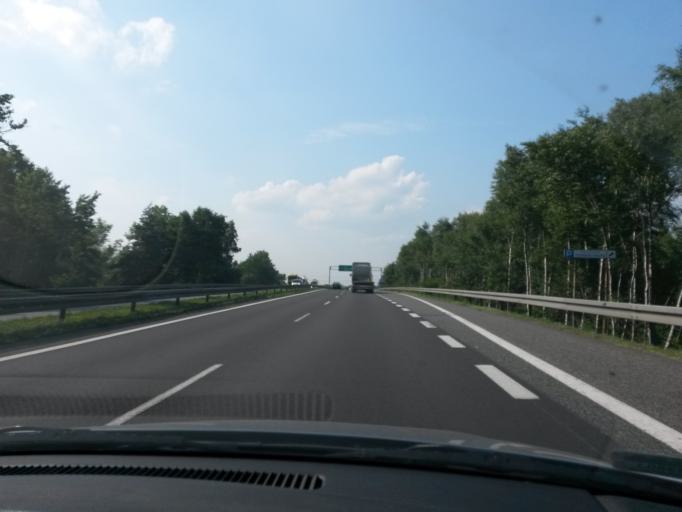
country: PL
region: Silesian Voivodeship
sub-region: Myslowice
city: Myslowice
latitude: 50.2230
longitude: 19.1715
